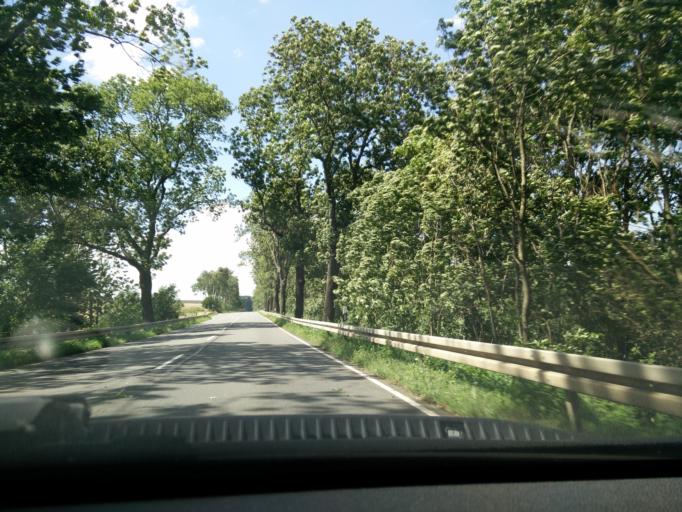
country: DE
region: Saxony
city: Penig
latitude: 50.9265
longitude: 12.7021
